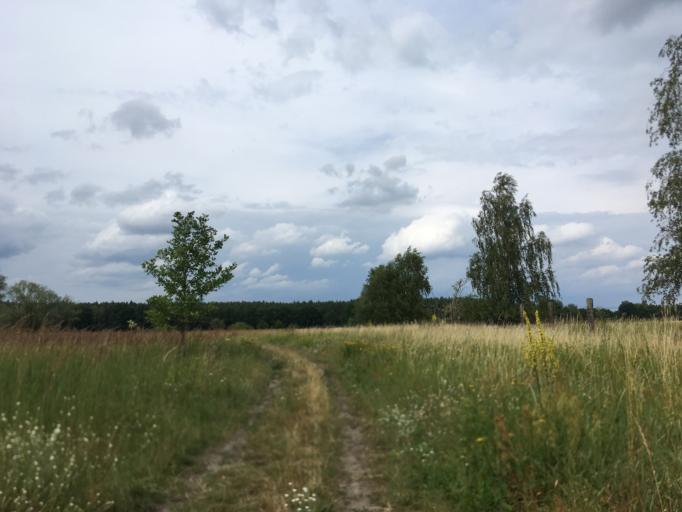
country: DE
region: Brandenburg
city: Bernau bei Berlin
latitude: 52.6379
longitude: 13.5900
